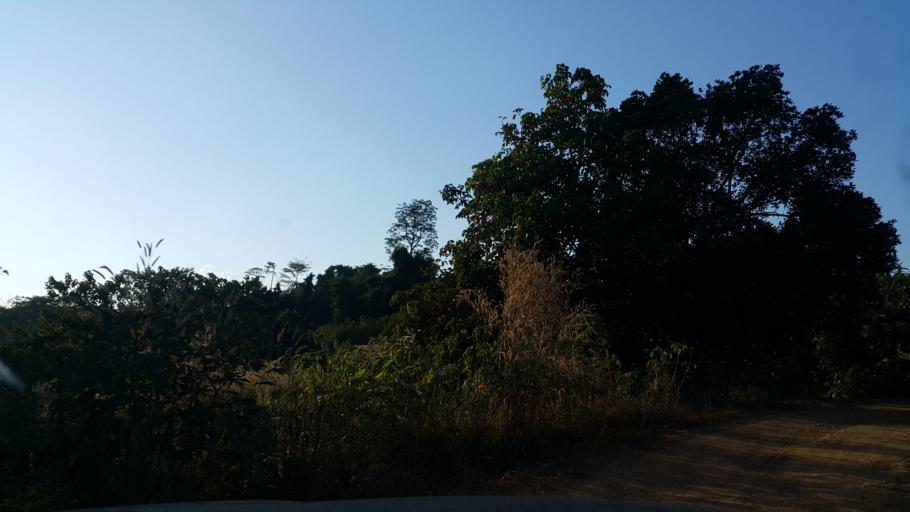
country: TH
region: Sukhothai
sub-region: Amphoe Si Satchanalai
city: Si Satchanalai
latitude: 17.5942
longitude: 99.6148
